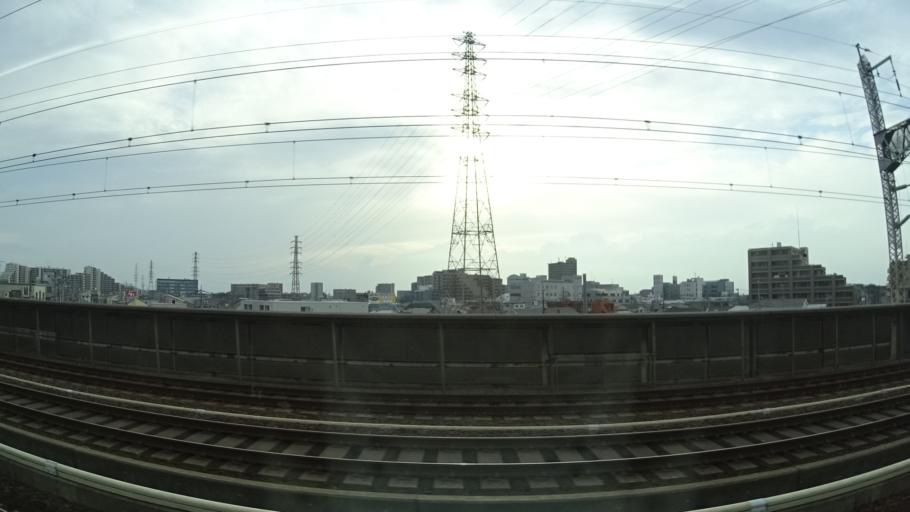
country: JP
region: Saitama
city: Ageoshimo
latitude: 35.9401
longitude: 139.6178
